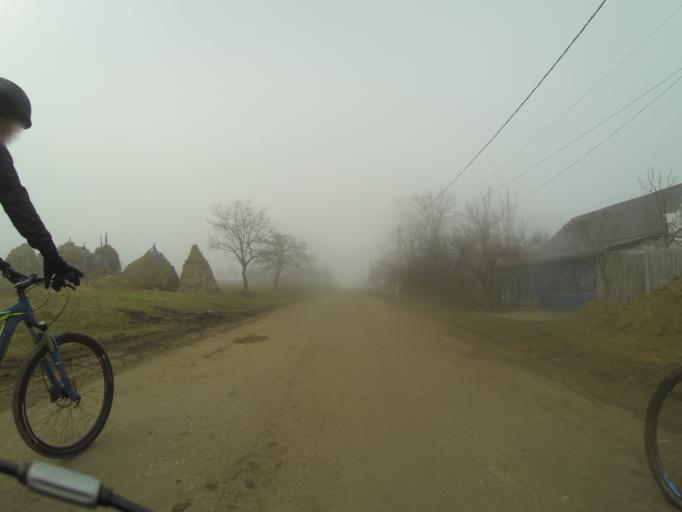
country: RO
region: Mehedinti
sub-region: Comuna Baclesu
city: Baclesu
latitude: 44.4809
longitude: 23.1066
